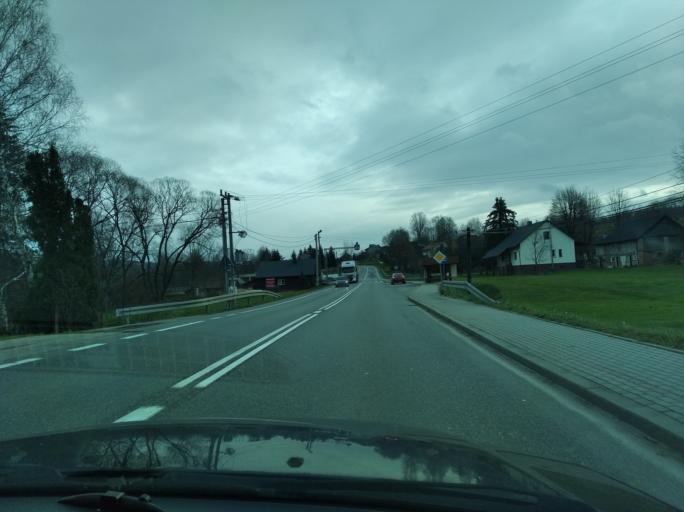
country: PL
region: Subcarpathian Voivodeship
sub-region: Powiat strzyzowski
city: Polomia
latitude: 49.8987
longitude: 21.8800
